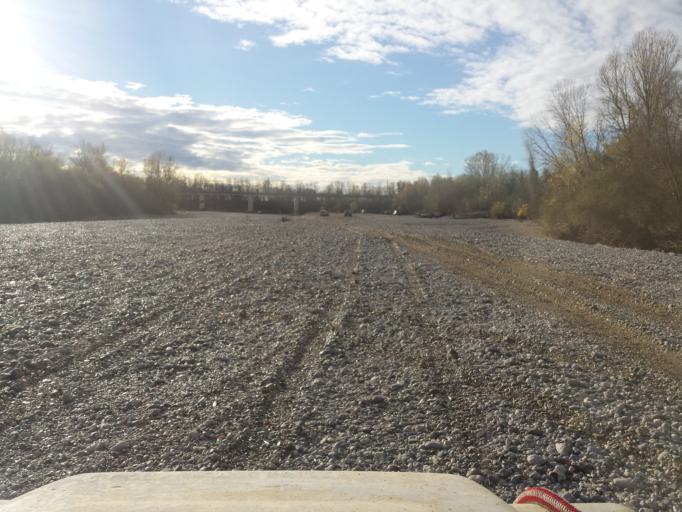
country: IT
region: Friuli Venezia Giulia
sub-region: Provincia di Udine
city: San Vito al Torre
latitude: 45.8969
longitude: 13.4028
